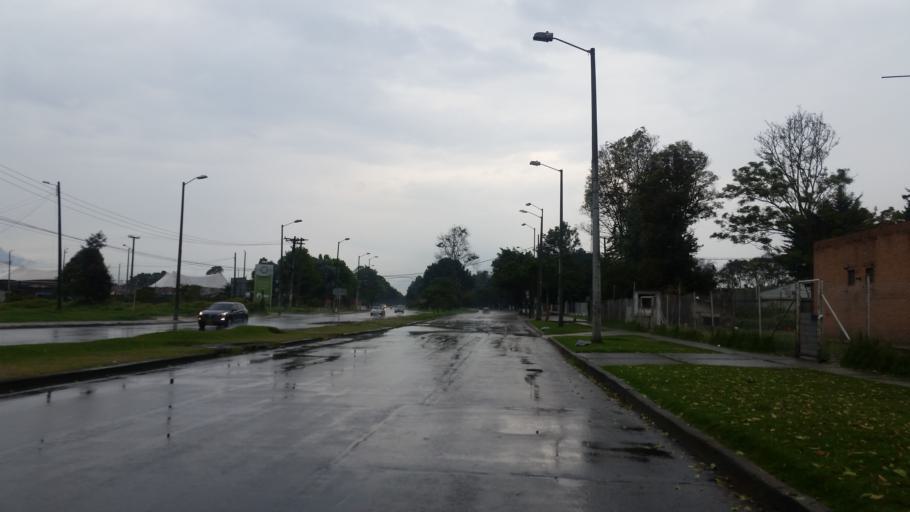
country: CO
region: Bogota D.C.
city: Bogota
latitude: 4.6667
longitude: -74.0852
